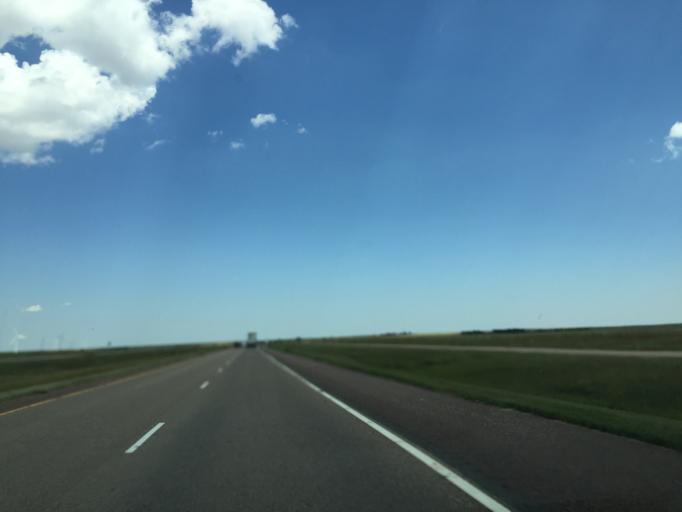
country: US
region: Colorado
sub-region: Lincoln County
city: Hugo
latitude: 39.2787
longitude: -103.4123
